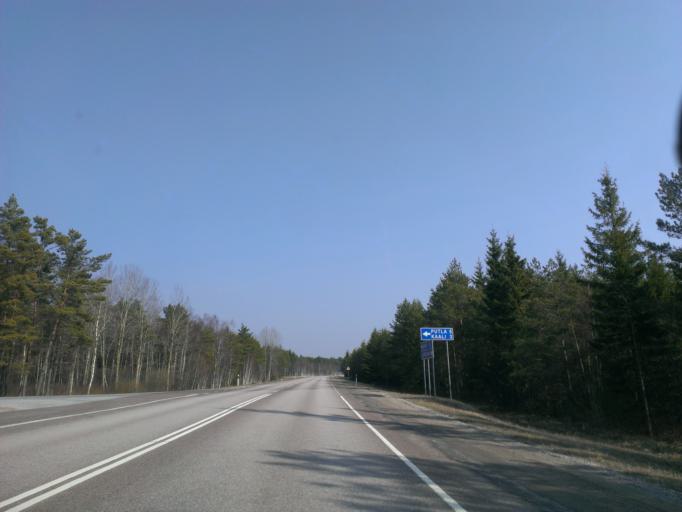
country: EE
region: Saare
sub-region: Kuressaare linn
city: Kuressaare
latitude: 58.3479
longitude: 22.6778
